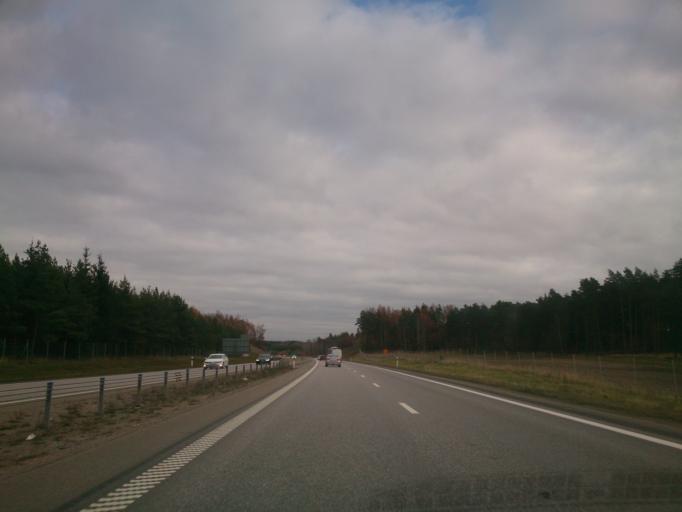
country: SE
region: OEstergoetland
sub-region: Norrkopings Kommun
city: Kimstad
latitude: 58.4920
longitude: 15.9628
